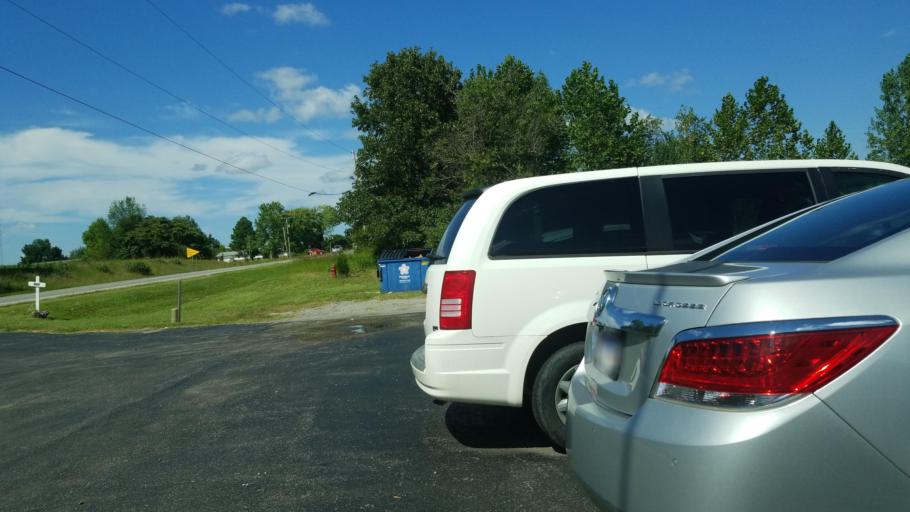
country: US
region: Illinois
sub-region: Williamson County
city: Marion
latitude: 37.7614
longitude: -88.9325
